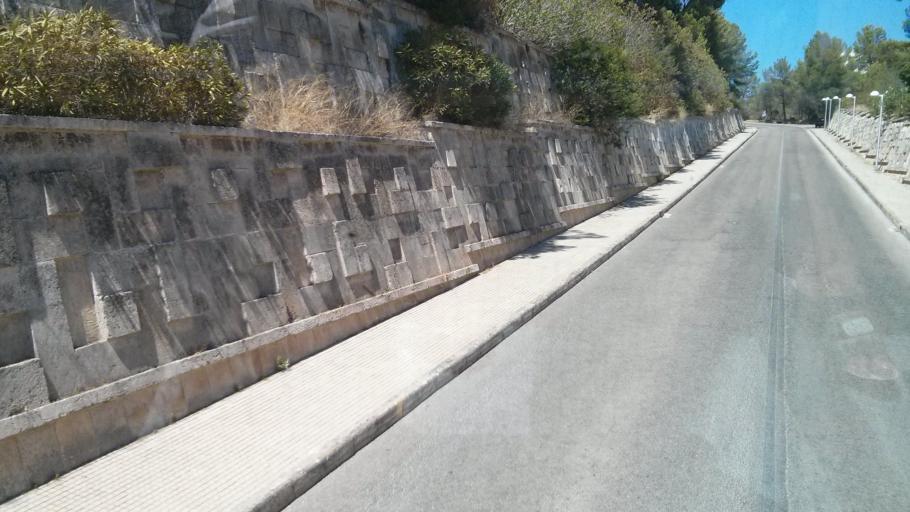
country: ES
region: Balearic Islands
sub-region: Illes Balears
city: Palma
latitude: 39.5674
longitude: 2.6237
